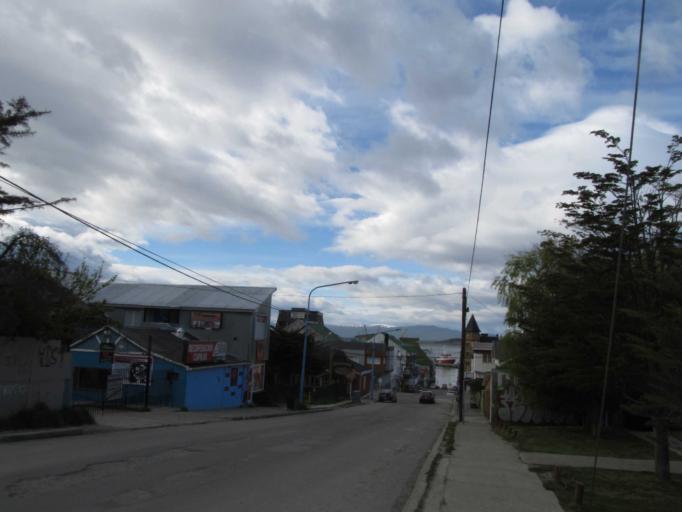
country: AR
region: Tierra del Fuego
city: Ushuaia
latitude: -54.8043
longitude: -68.3035
